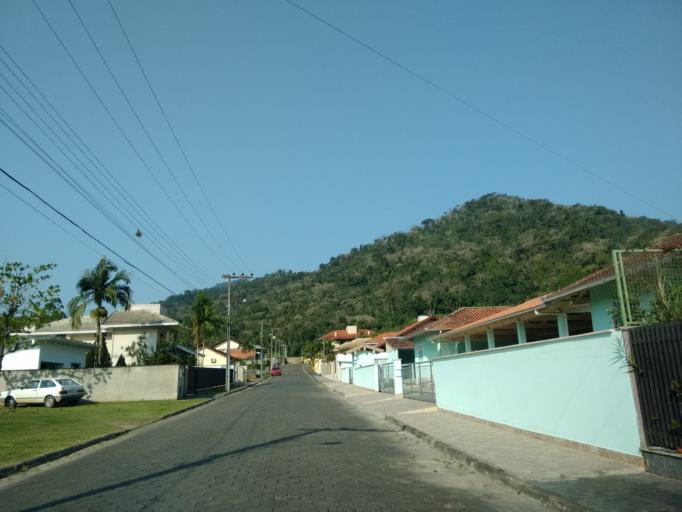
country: BR
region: Santa Catarina
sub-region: Pomerode
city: Pomerode
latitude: -26.7472
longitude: -49.1634
